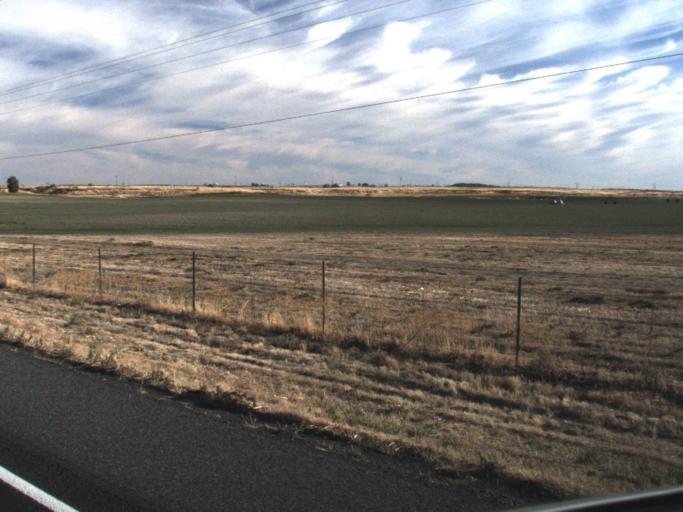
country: US
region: Washington
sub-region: Franklin County
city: Basin City
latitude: 46.6137
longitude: -119.0062
